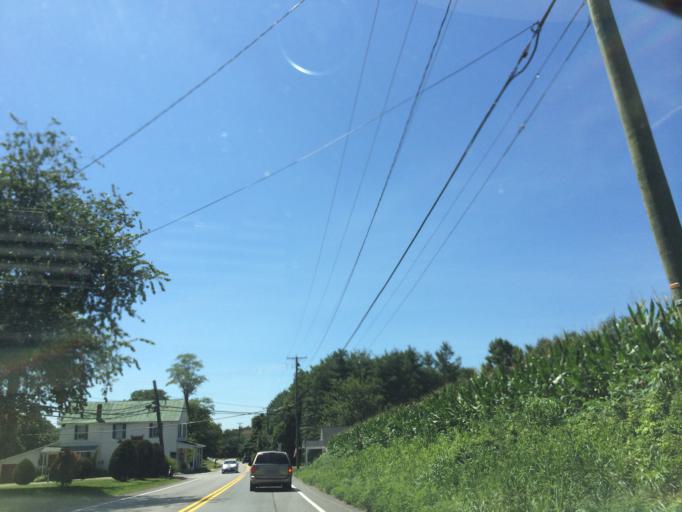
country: US
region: Maryland
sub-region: Carroll County
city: Sykesville
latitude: 39.3213
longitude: -76.9269
